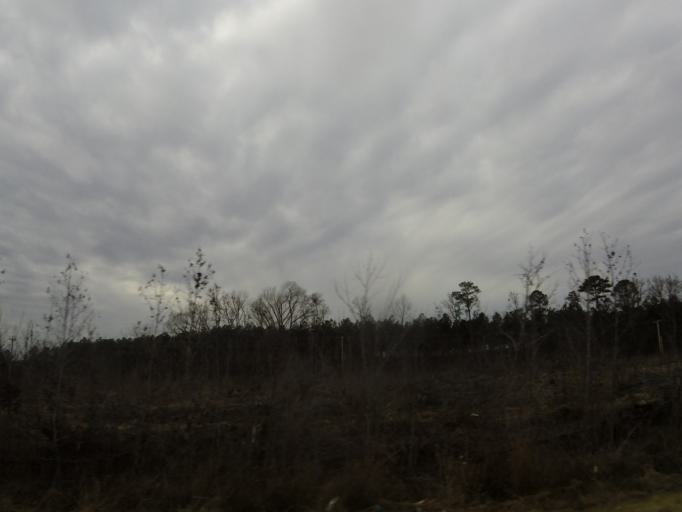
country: US
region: North Carolina
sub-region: Northampton County
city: Jackson
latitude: 36.2910
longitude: -77.2742
